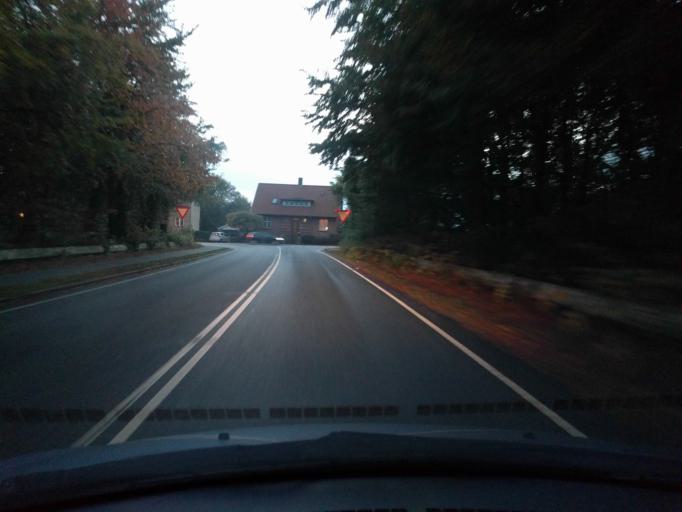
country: DK
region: South Denmark
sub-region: Svendborg Kommune
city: Svendborg
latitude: 55.0529
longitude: 10.5934
